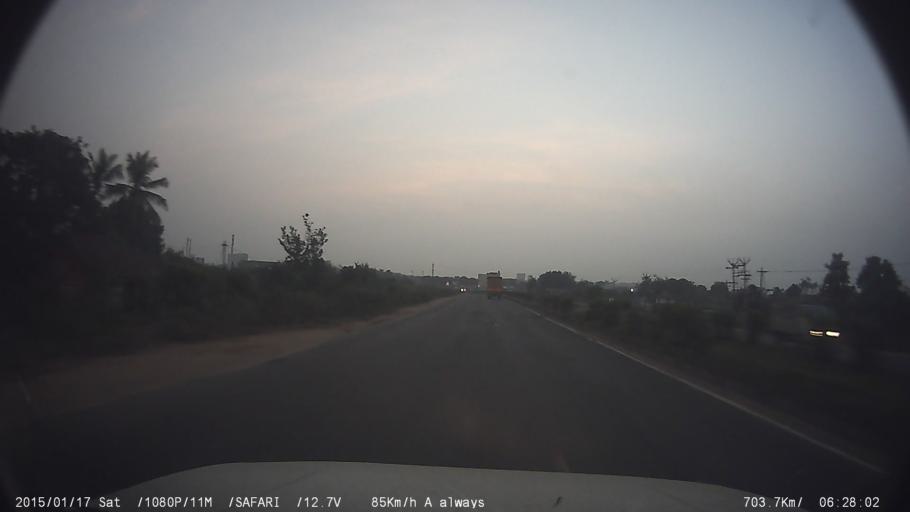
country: IN
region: Tamil Nadu
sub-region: Kancheepuram
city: Sriperumbudur
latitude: 12.9337
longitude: 79.9043
